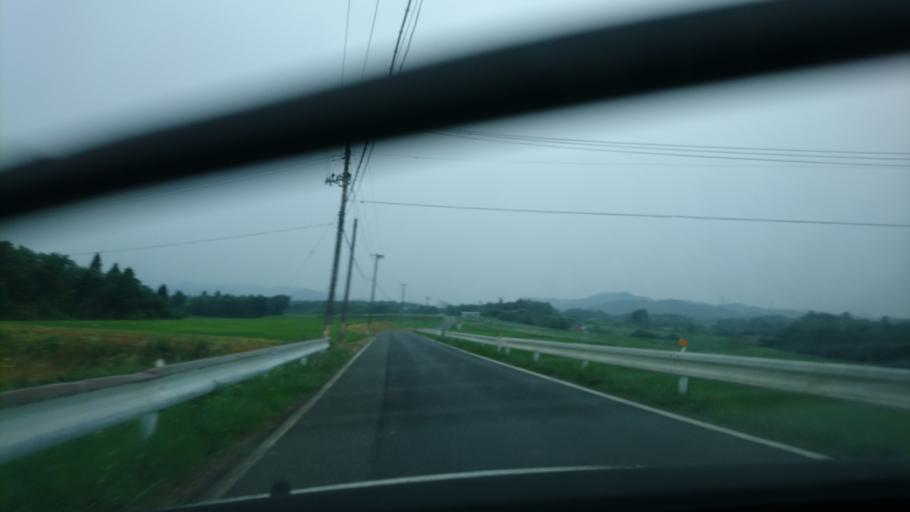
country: JP
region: Iwate
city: Ichinoseki
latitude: 38.9029
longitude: 141.1962
